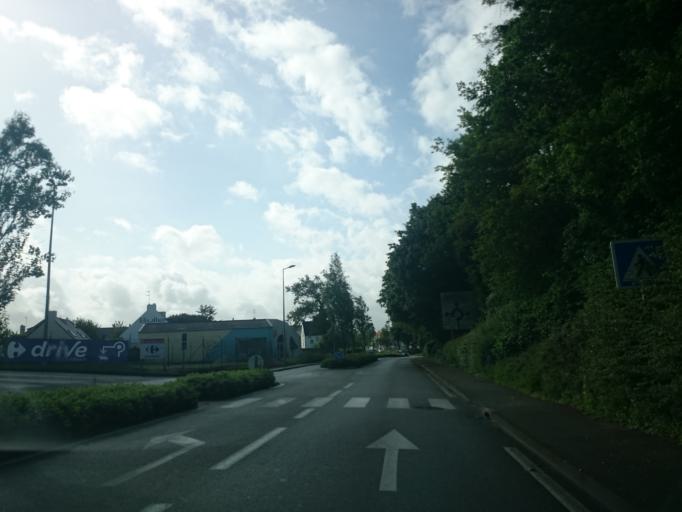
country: FR
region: Brittany
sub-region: Departement du Morbihan
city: Plescop
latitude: 47.6575
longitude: -2.7926
